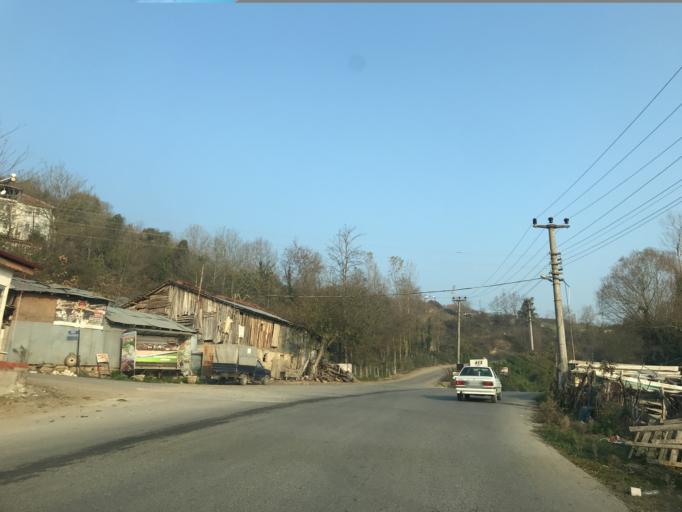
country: TR
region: Duzce
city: Cumayeri
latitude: 40.8885
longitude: 30.9516
